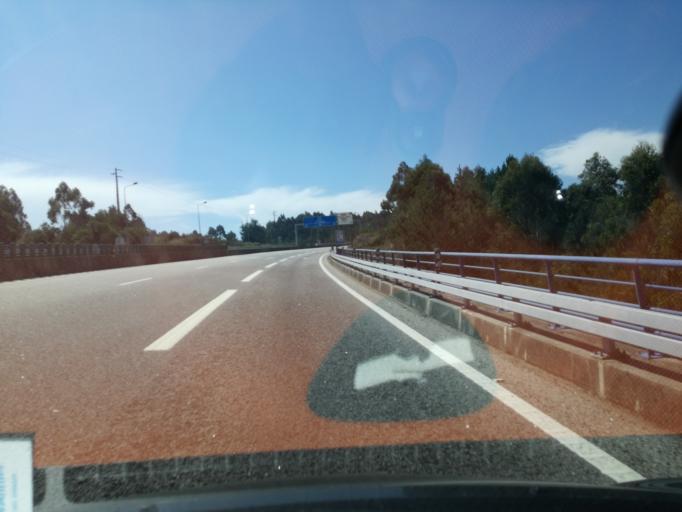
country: PT
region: Viana do Castelo
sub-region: Caminha
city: Vila Praia de Ancora
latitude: 41.8513
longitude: -8.7743
